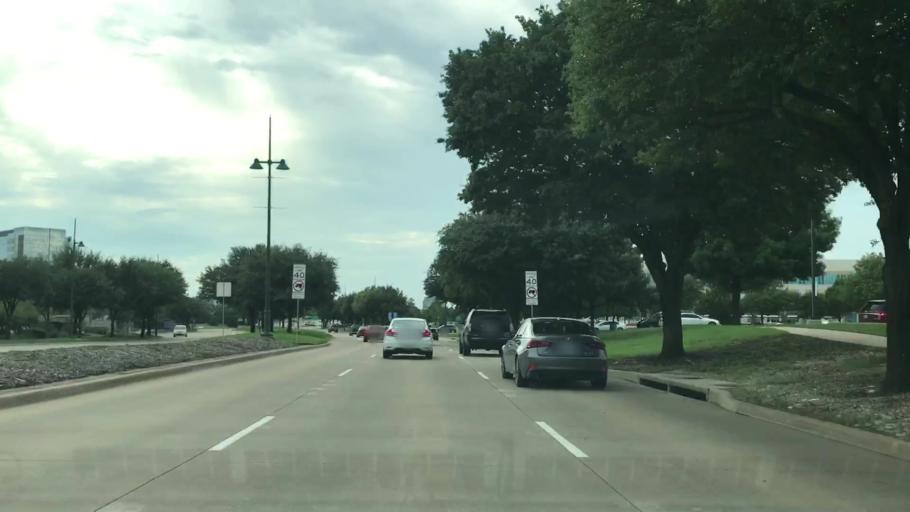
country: US
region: Texas
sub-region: Collin County
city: Frisco
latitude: 33.1072
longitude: -96.8177
